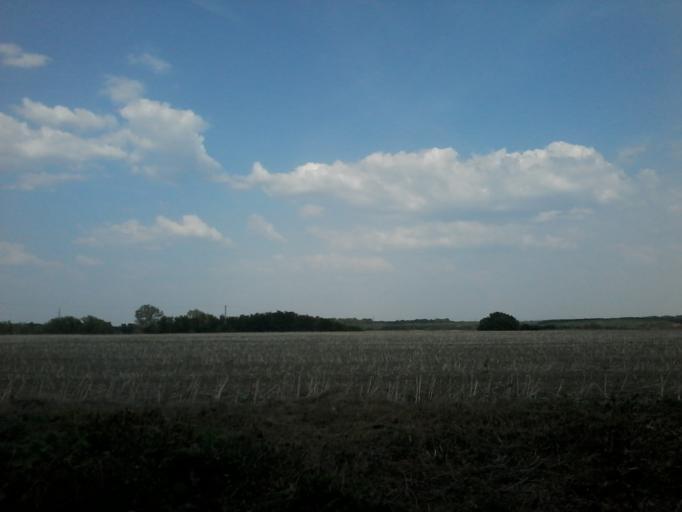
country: HU
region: Vas
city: Celldomolk
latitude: 47.2111
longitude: 17.1039
